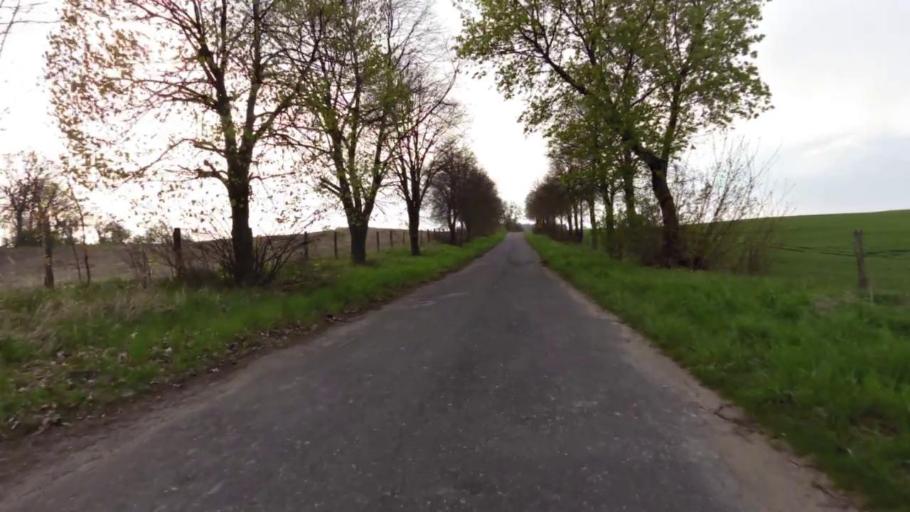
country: PL
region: West Pomeranian Voivodeship
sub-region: Powiat mysliborski
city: Mysliborz
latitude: 52.8911
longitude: 14.7882
